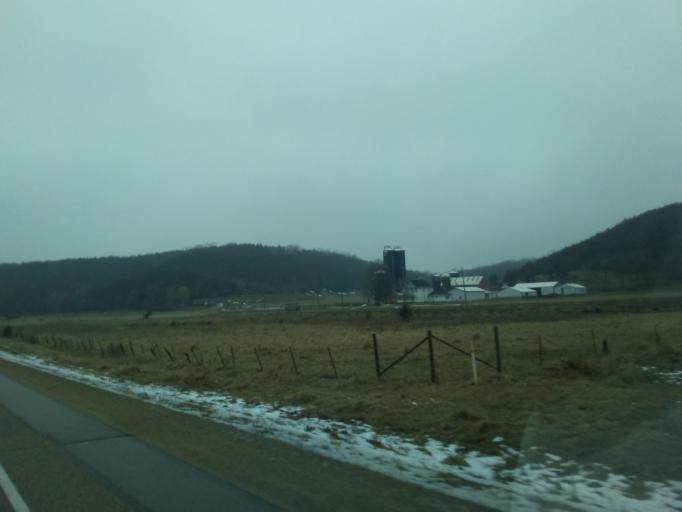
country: US
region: Wisconsin
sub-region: Dane County
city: Black Earth
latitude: 43.1325
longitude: -89.7259
